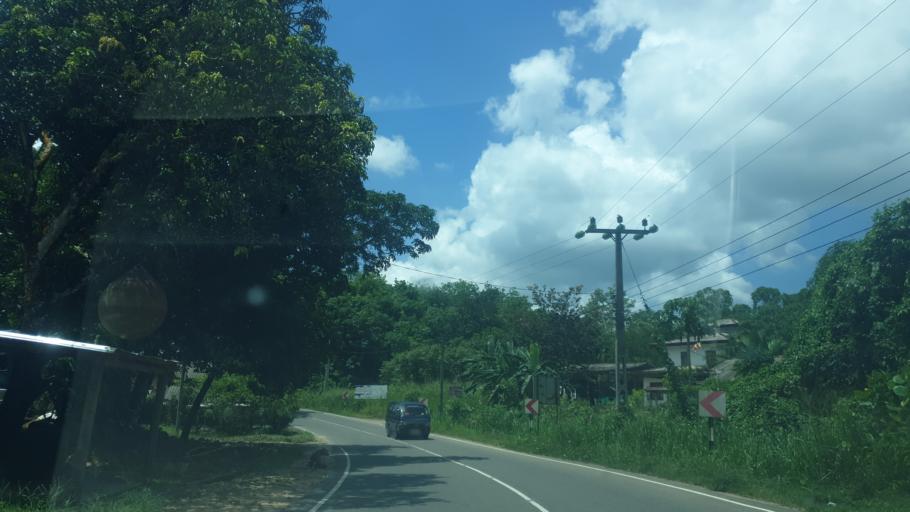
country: LK
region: Western
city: Horawala Junction
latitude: 6.5143
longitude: 80.2405
